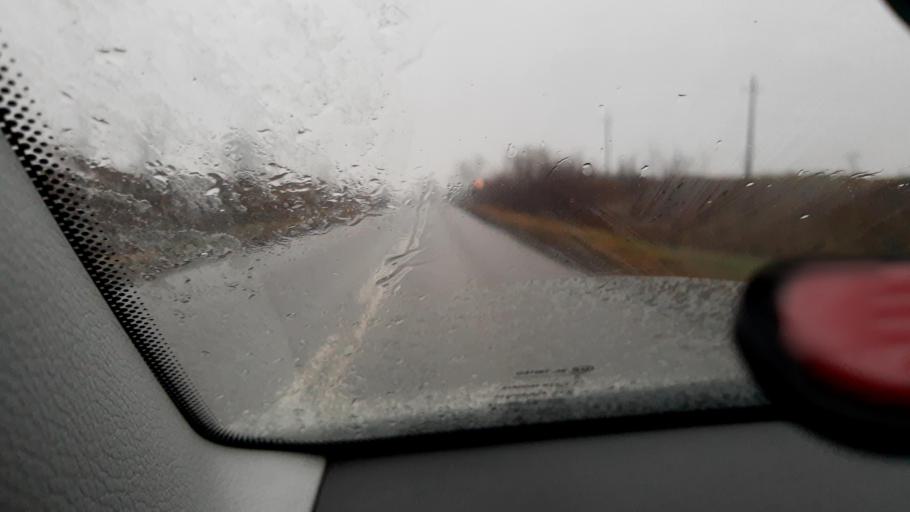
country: RU
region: Bashkortostan
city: Iglino
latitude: 54.9004
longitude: 56.1933
